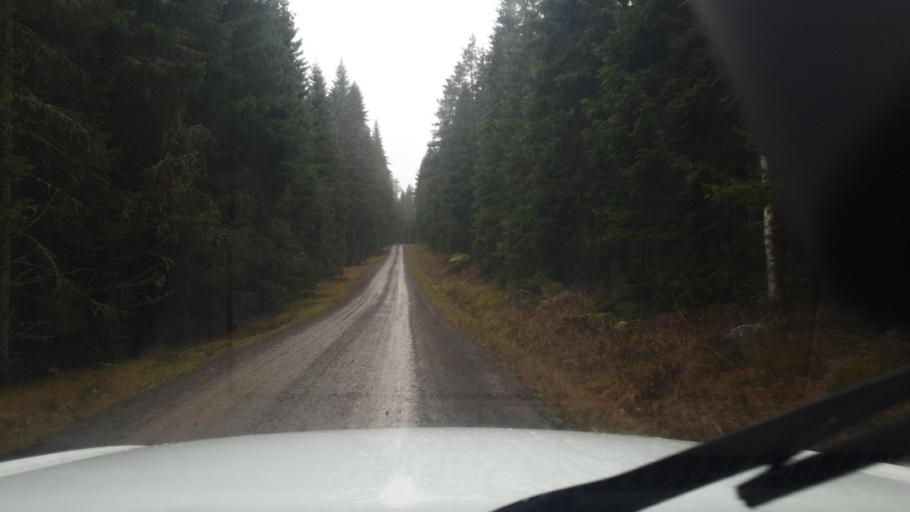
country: SE
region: Vaermland
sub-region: Sunne Kommun
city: Sunne
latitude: 59.8586
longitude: 12.8415
